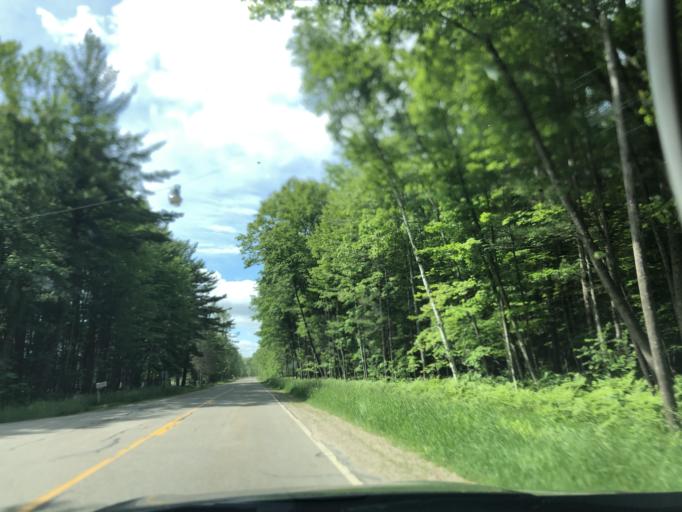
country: US
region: Michigan
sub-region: Roscommon County
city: Houghton Lake
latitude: 44.3577
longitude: -84.8549
